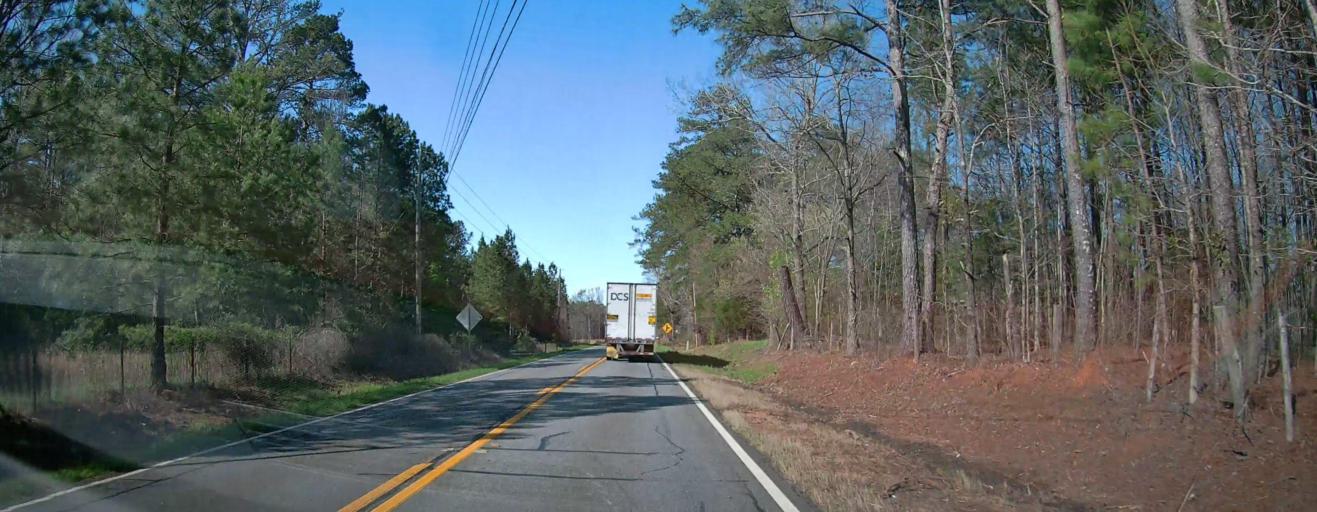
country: US
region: Georgia
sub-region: Monroe County
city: Forsyth
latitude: 33.1070
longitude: -83.9448
